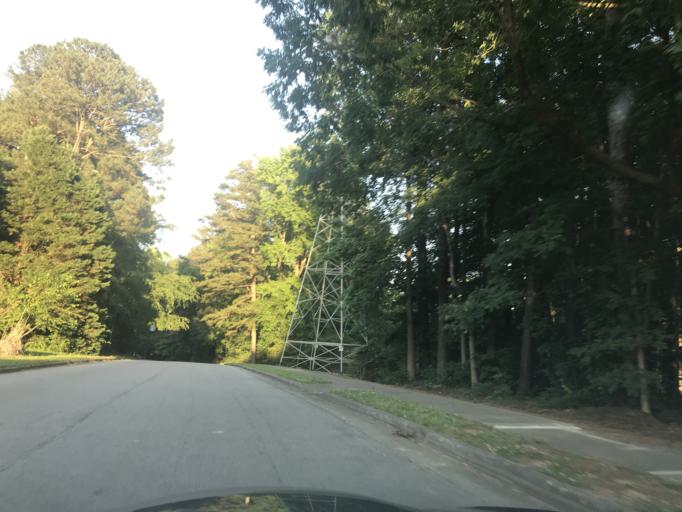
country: US
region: North Carolina
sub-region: Wake County
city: Raleigh
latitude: 35.7493
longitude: -78.6640
